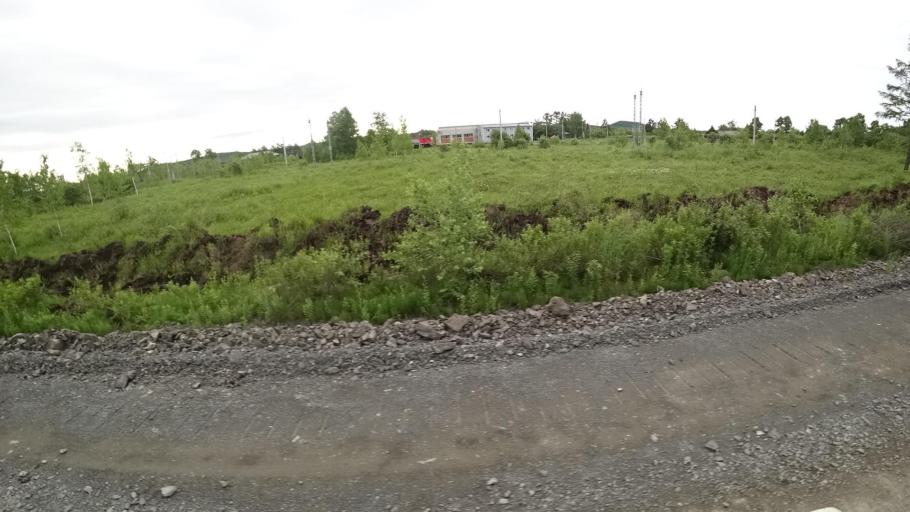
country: RU
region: Khabarovsk Krai
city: Amursk
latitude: 49.9019
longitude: 136.1372
